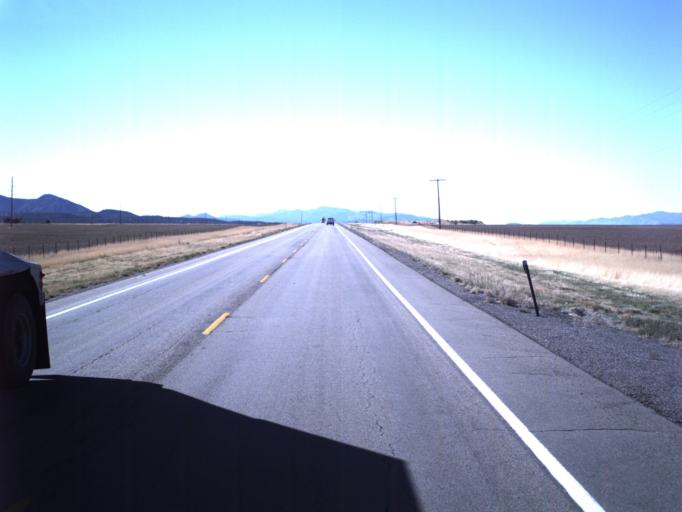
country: US
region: Utah
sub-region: Juab County
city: Nephi
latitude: 39.4751
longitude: -111.8932
